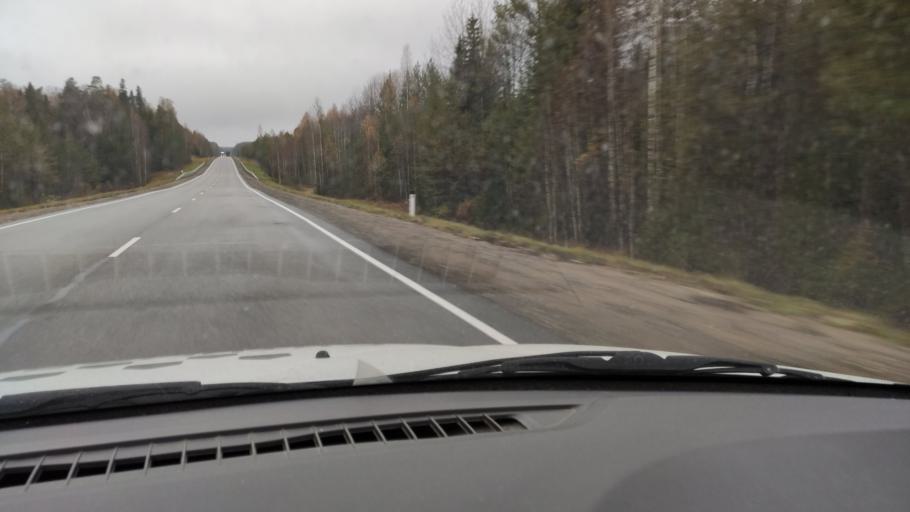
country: RU
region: Kirov
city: Chernaya Kholunitsa
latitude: 58.8226
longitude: 51.8018
